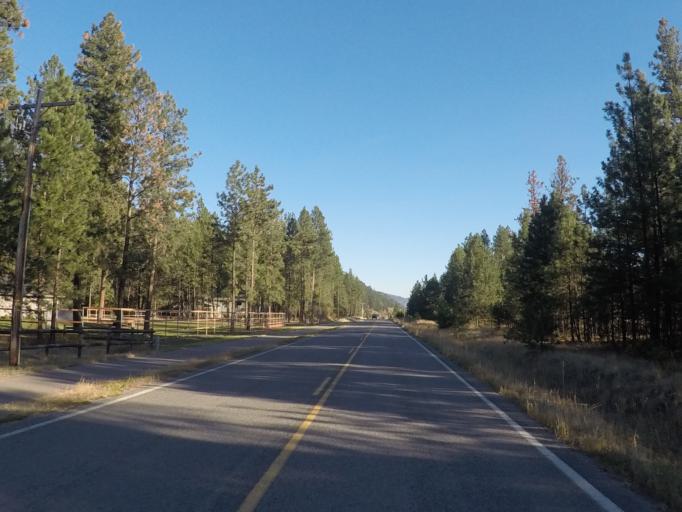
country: US
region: Montana
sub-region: Missoula County
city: Bonner-West Riverside
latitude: 46.8395
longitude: -113.8328
